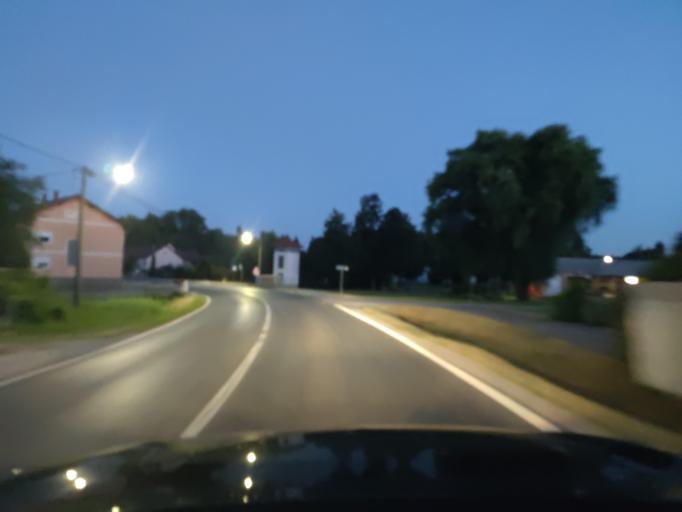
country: HR
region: Medimurska
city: Vratisinec
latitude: 46.4731
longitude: 16.4230
